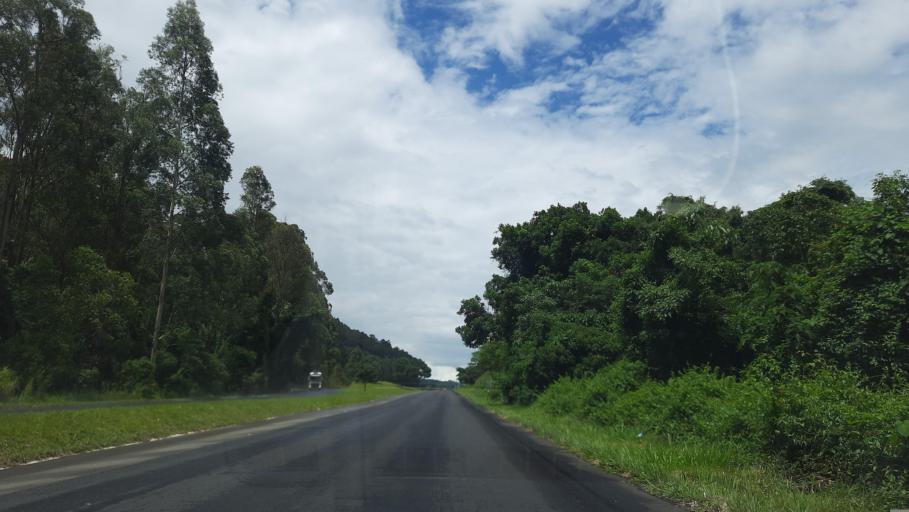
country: BR
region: Minas Gerais
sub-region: Pocos De Caldas
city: Pocos de Caldas
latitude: -21.8025
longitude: -46.6507
